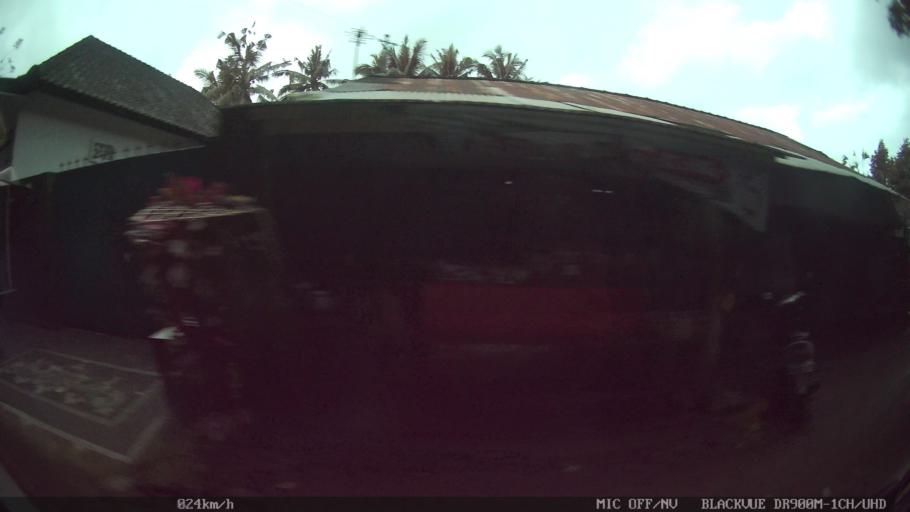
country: ID
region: Bali
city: Banjar Wangsian
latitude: -8.4353
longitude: 115.4260
